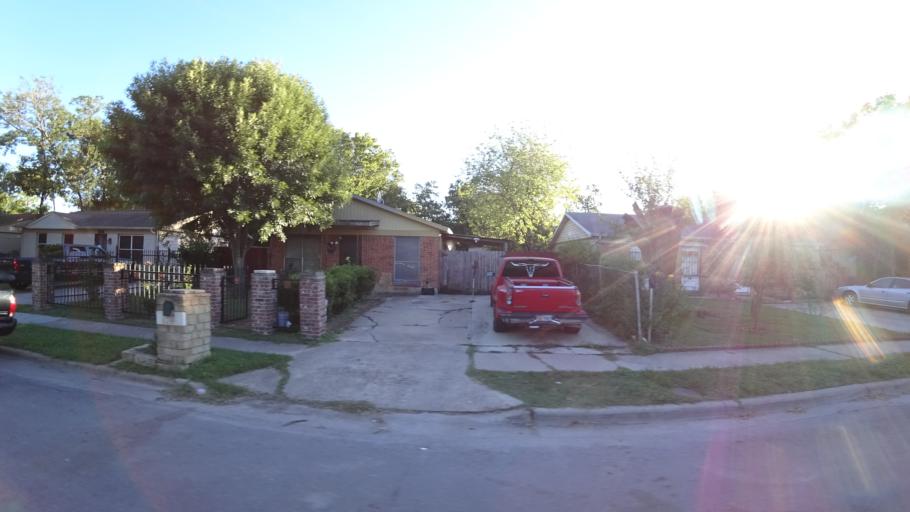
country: US
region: Texas
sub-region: Travis County
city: Austin
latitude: 30.2309
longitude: -97.7004
